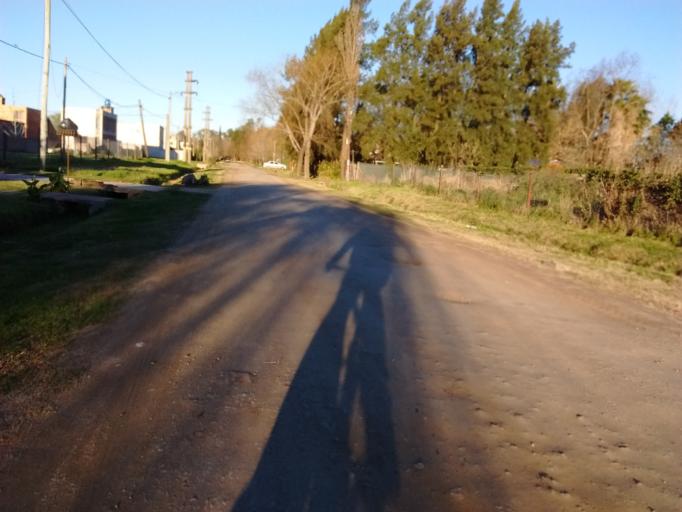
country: AR
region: Santa Fe
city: Funes
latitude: -32.9124
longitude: -60.8547
